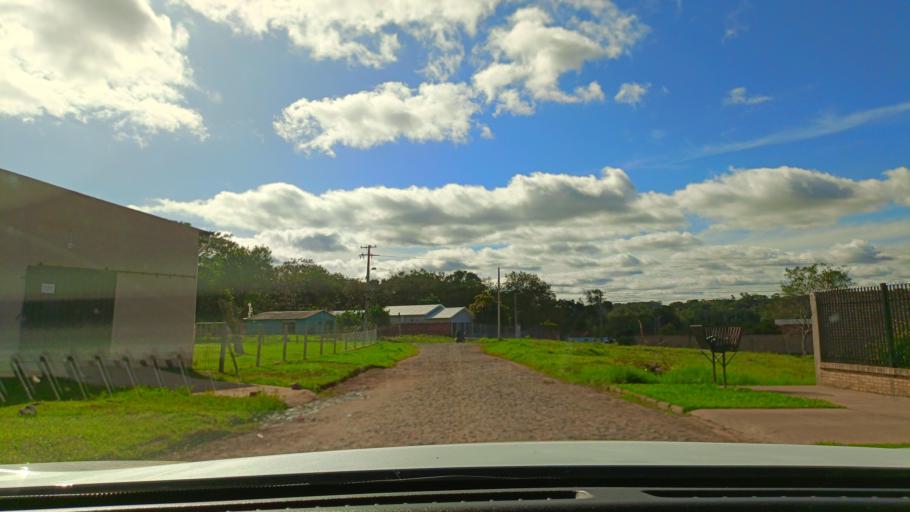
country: PY
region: San Pedro
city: Guayaybi
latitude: -24.6571
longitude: -56.4429
